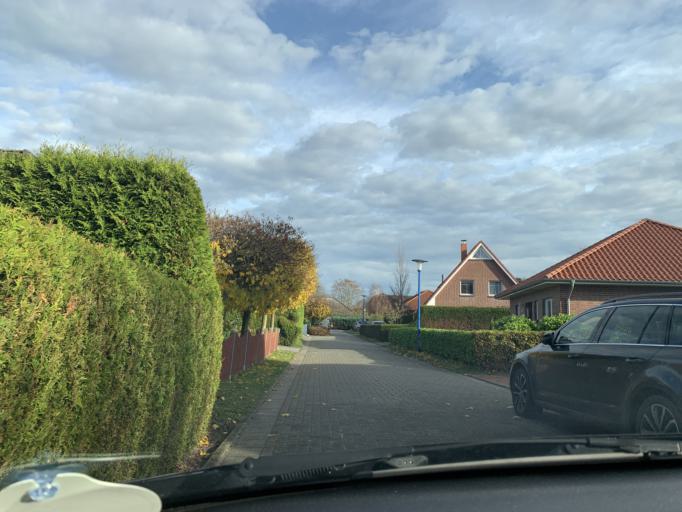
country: DE
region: Lower Saxony
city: Apen
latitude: 53.2183
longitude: 7.8120
